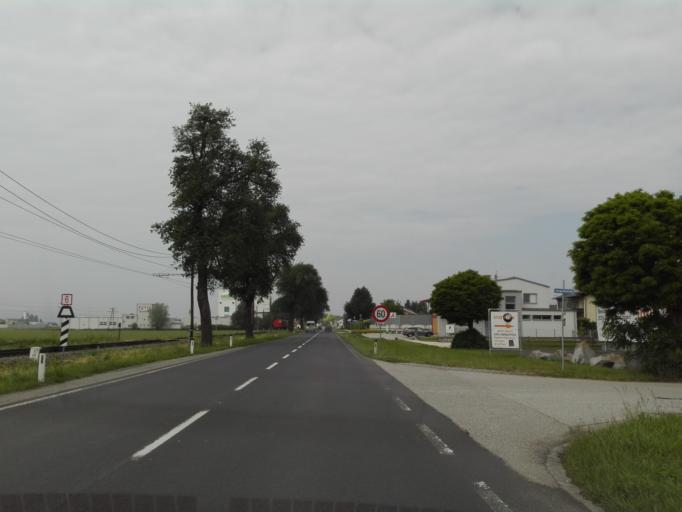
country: AT
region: Upper Austria
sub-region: Politischer Bezirk Urfahr-Umgebung
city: Goldworth
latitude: 48.2887
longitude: 14.1239
